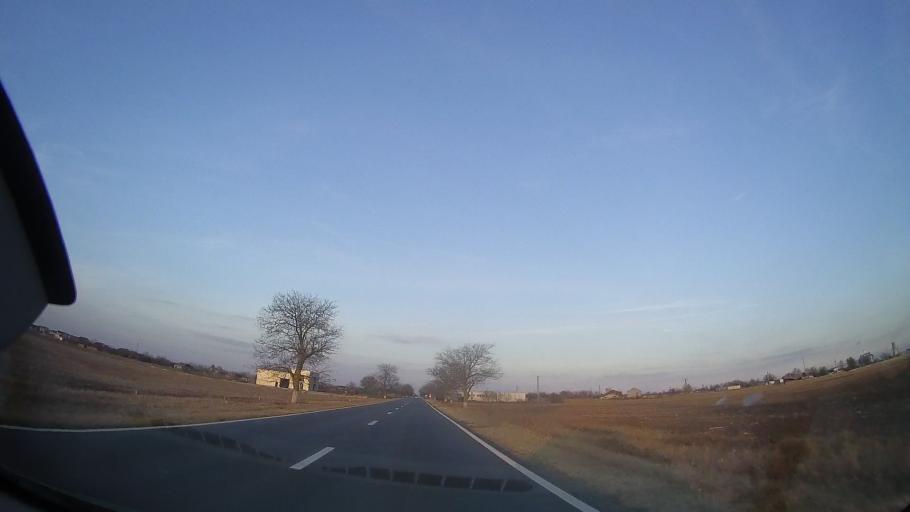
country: RO
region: Constanta
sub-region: Comuna Topraisar
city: Topraisar
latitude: 44.0056
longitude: 28.4411
